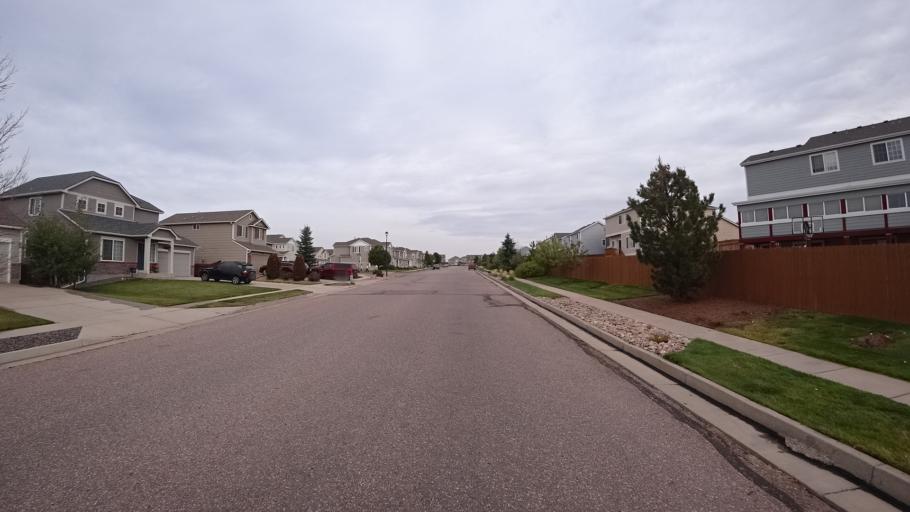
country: US
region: Colorado
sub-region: El Paso County
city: Cimarron Hills
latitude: 38.9236
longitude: -104.7105
